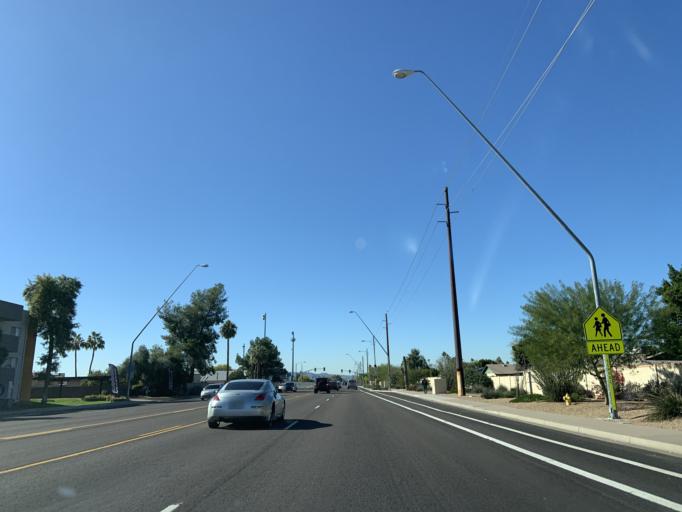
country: US
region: Arizona
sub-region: Maricopa County
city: San Carlos
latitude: 33.3643
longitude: -111.8618
